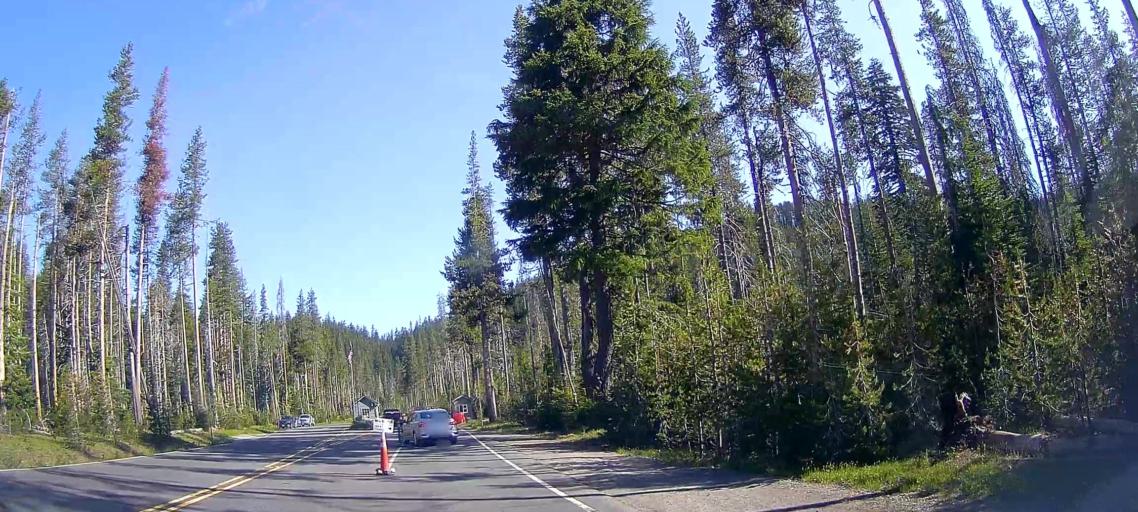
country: US
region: Oregon
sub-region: Jackson County
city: Shady Cove
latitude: 42.8681
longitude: -122.1688
